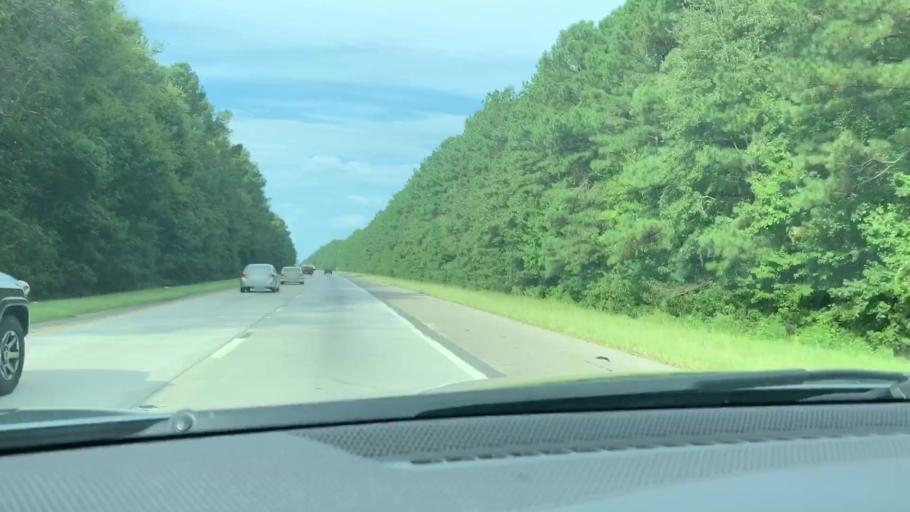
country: US
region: South Carolina
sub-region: Colleton County
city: Walterboro
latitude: 32.9638
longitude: -80.6775
